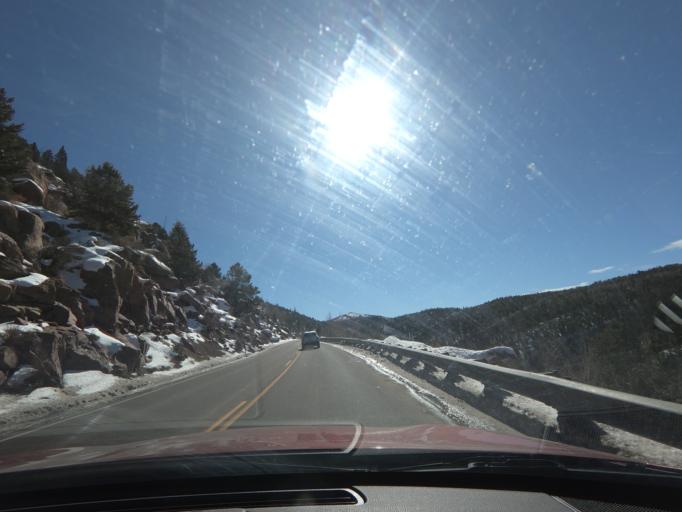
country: US
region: Colorado
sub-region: Teller County
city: Cripple Creek
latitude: 38.8121
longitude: -105.1277
